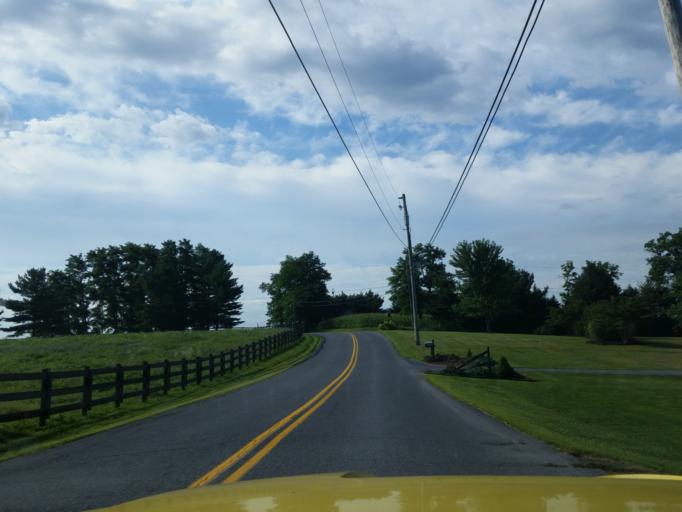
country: US
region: Pennsylvania
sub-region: Lebanon County
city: Fredericksburg
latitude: 40.4584
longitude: -76.4370
